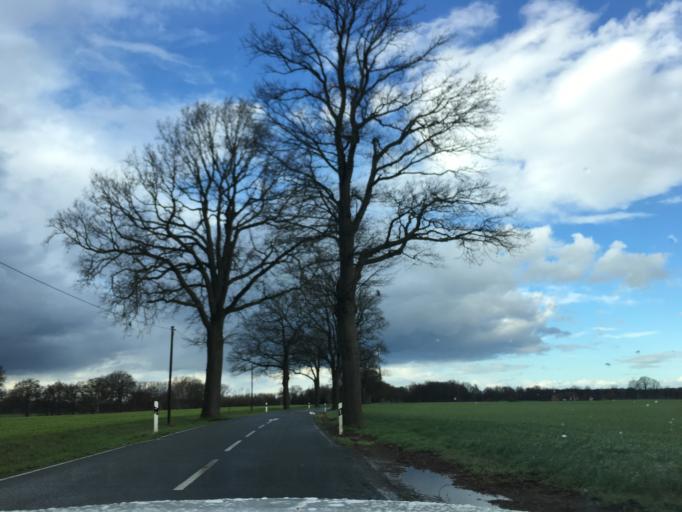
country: DE
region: North Rhine-Westphalia
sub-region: Regierungsbezirk Munster
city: Isselburg
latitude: 51.7960
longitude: 6.4799
